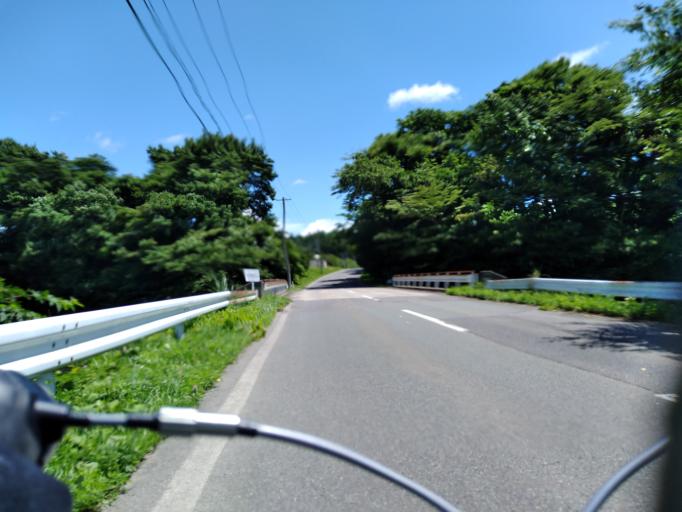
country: JP
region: Iwate
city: Shizukuishi
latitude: 39.7615
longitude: 140.9664
